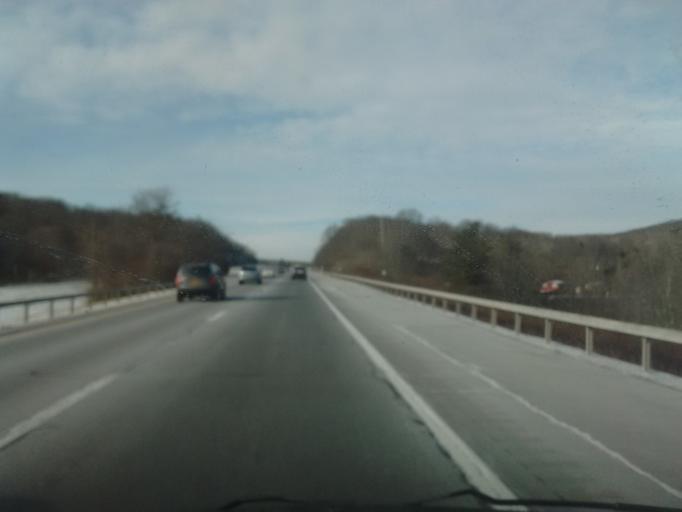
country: US
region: New York
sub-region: Putnam County
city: Lake Carmel
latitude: 41.4505
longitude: -73.6375
